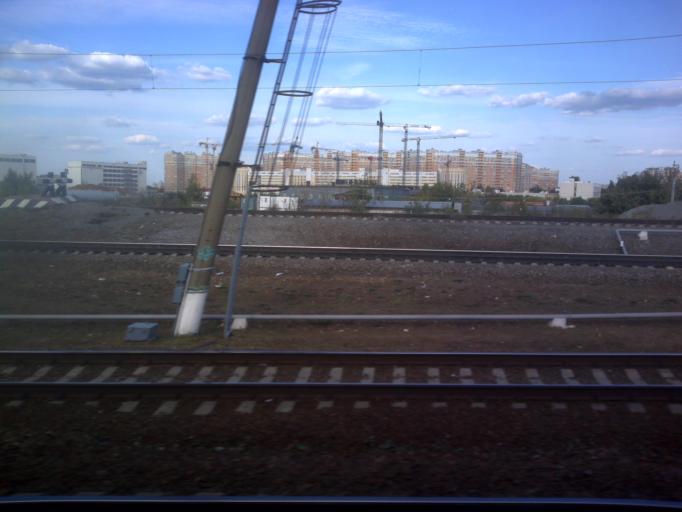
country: RU
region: Moskovskaya
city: Biryulevo Zapadnoye
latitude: 55.6020
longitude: 37.6484
